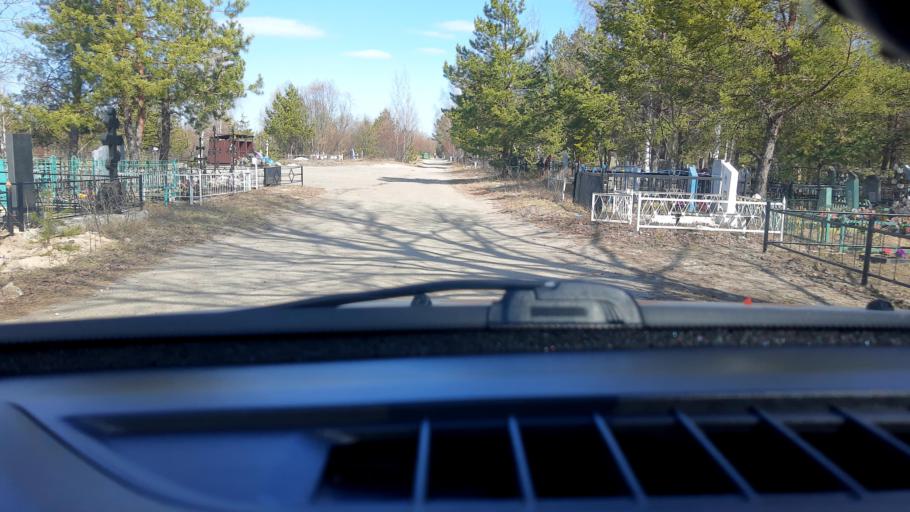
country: RU
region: Nizjnij Novgorod
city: Gorbatovka
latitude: 56.3548
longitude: 43.7701
